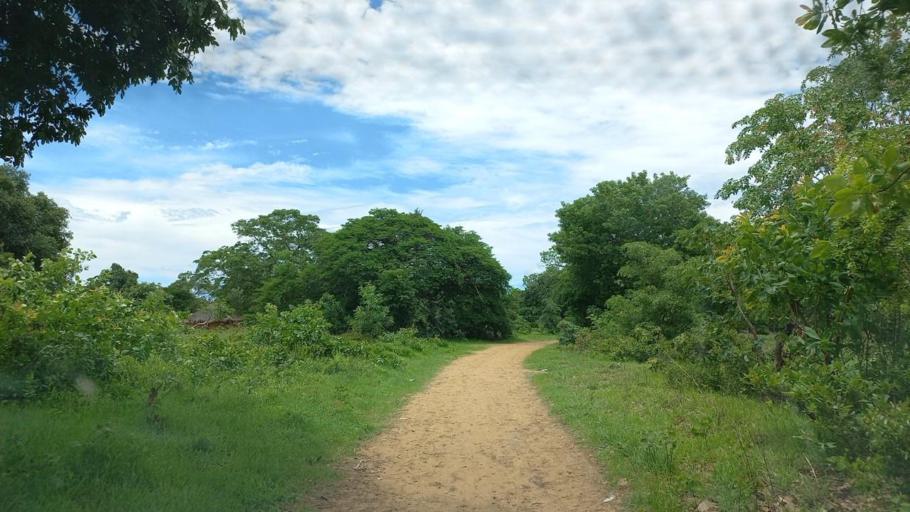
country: ZM
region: North-Western
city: Kabompo
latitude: -13.6238
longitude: 24.1846
